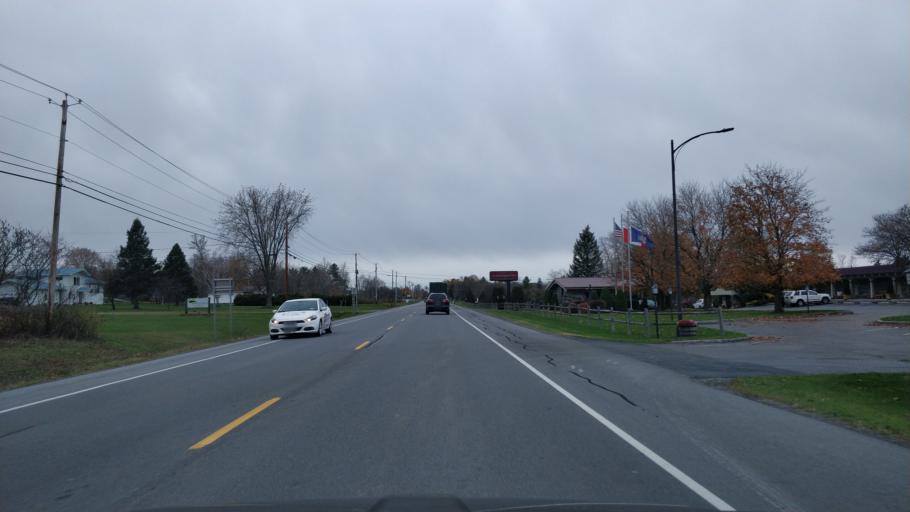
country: CA
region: Ontario
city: Prescott
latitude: 44.6657
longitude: -75.5379
